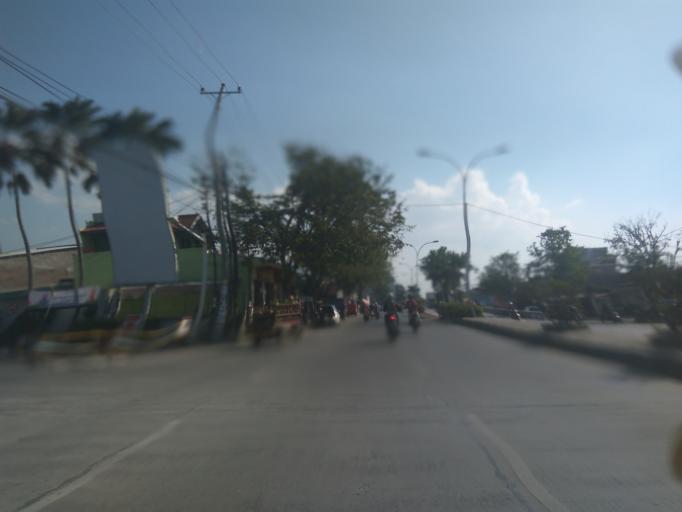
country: ID
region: Central Java
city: Semarang
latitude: -6.9594
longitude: 110.4440
